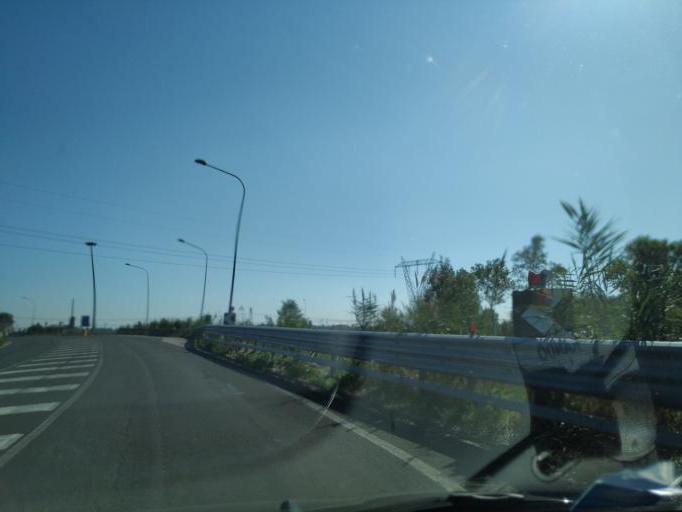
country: IT
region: Emilia-Romagna
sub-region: Provincia di Bologna
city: Decima
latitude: 44.6741
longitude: 11.2101
